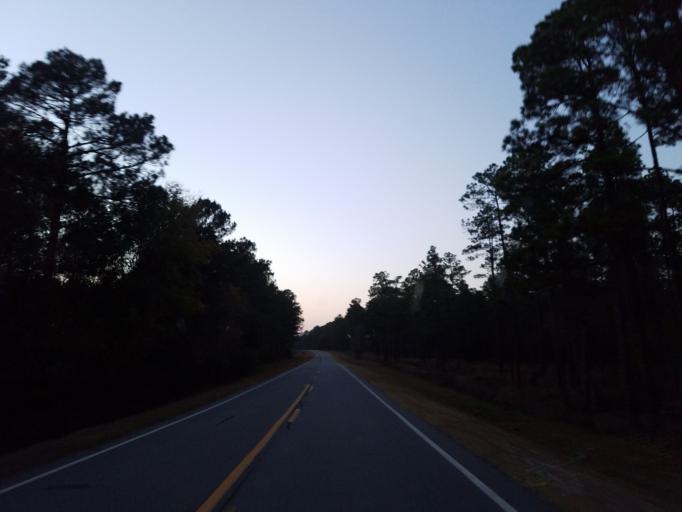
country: US
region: Georgia
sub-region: Wilcox County
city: Rochelle
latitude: 31.8204
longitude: -83.5407
